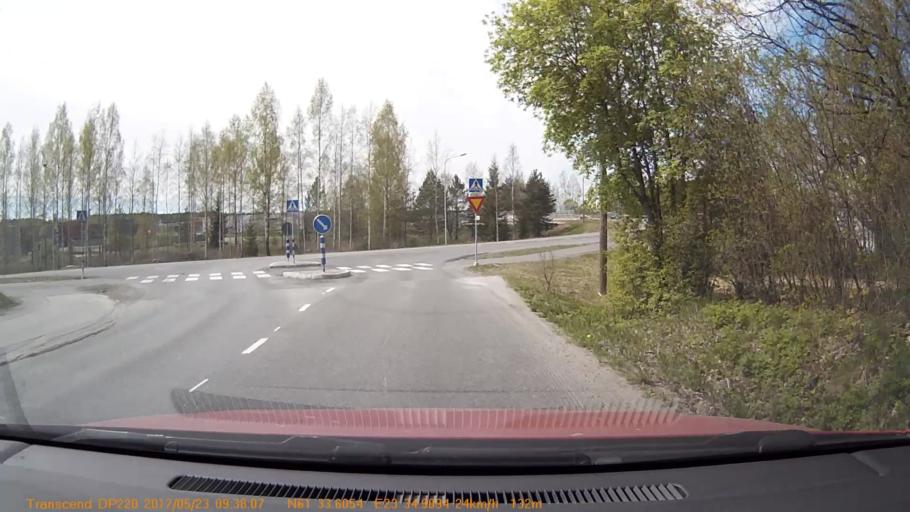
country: FI
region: Pirkanmaa
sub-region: Tampere
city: Yloejaervi
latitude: 61.5602
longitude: 23.5818
